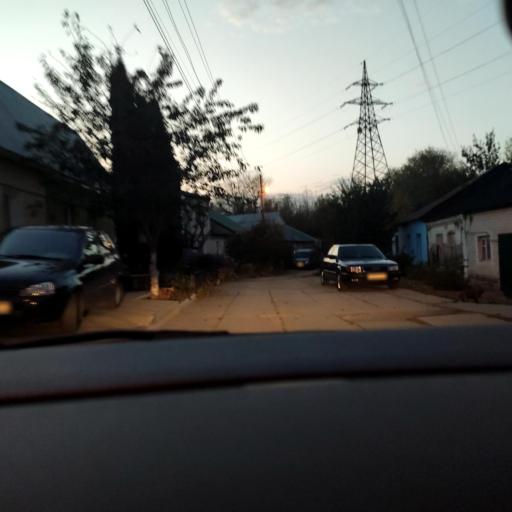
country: RU
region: Voronezj
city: Voronezh
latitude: 51.6820
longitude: 39.1588
